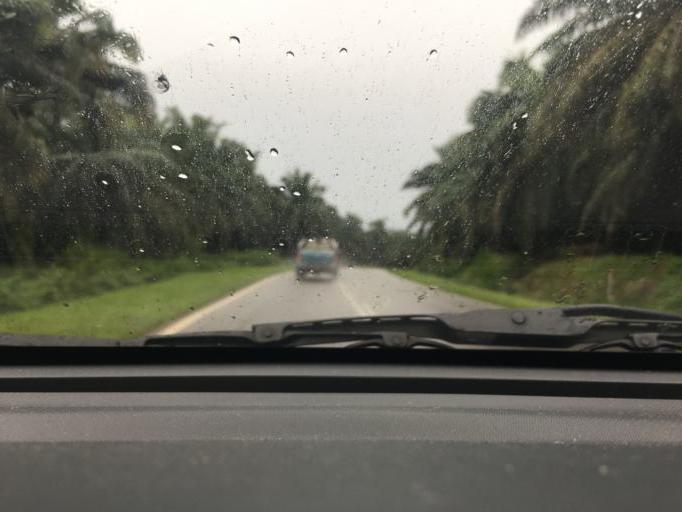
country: MY
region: Kedah
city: Sungai Petani
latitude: 5.6509
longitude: 100.6336
